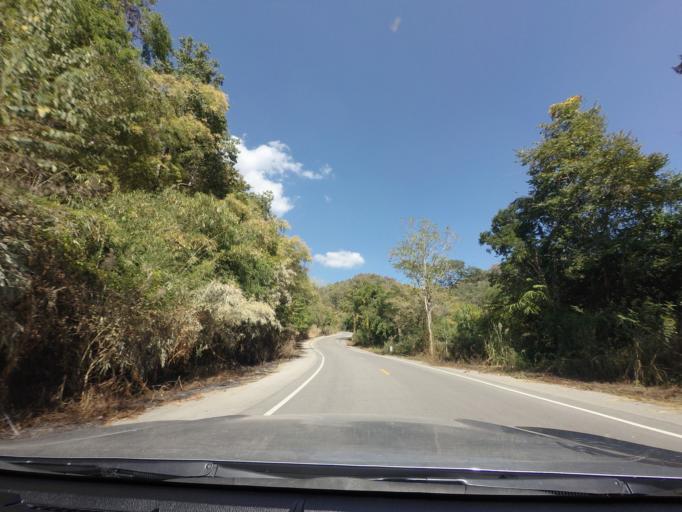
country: TH
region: Lampang
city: Chae Hom
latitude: 18.5562
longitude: 99.6265
